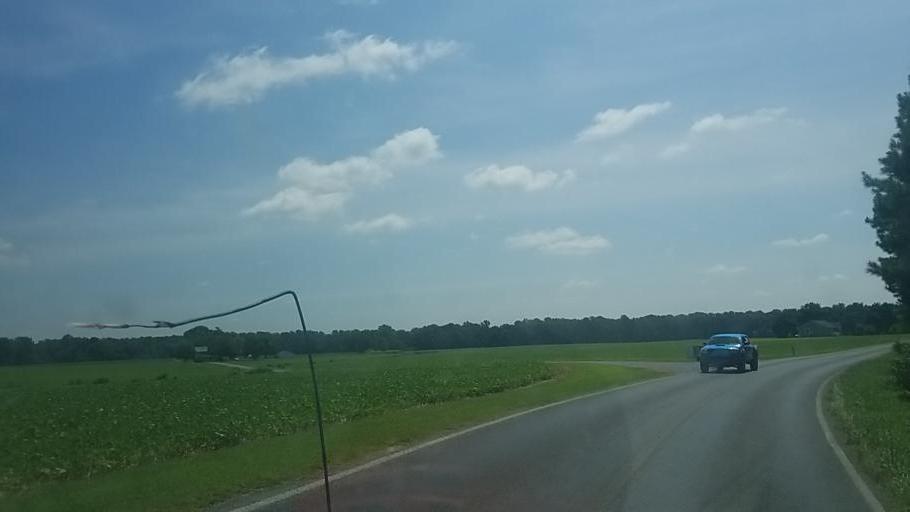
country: US
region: Maryland
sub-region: Caroline County
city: Ridgely
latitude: 38.8914
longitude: -75.9290
